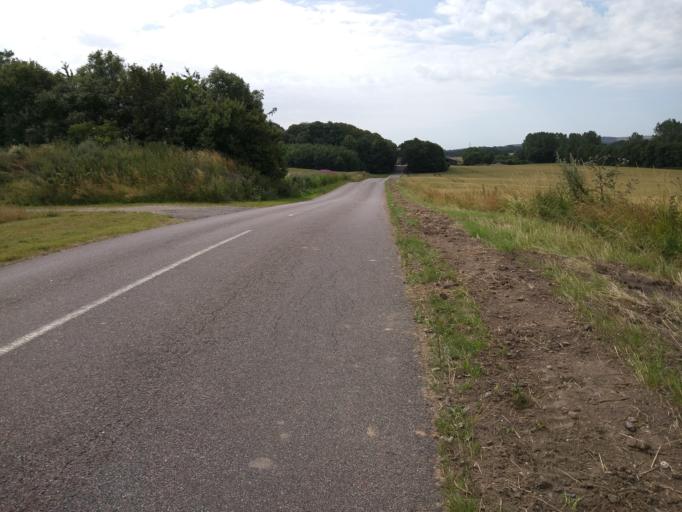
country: DK
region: Zealand
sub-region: Kalundborg Kommune
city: Svebolle
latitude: 55.7007
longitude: 11.3054
